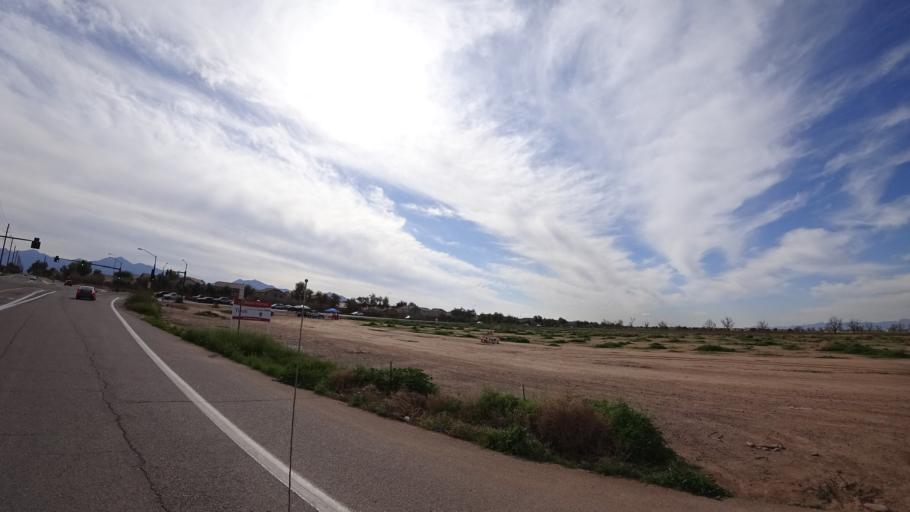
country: US
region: Arizona
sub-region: Maricopa County
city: Tolleson
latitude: 33.4221
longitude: -112.2556
